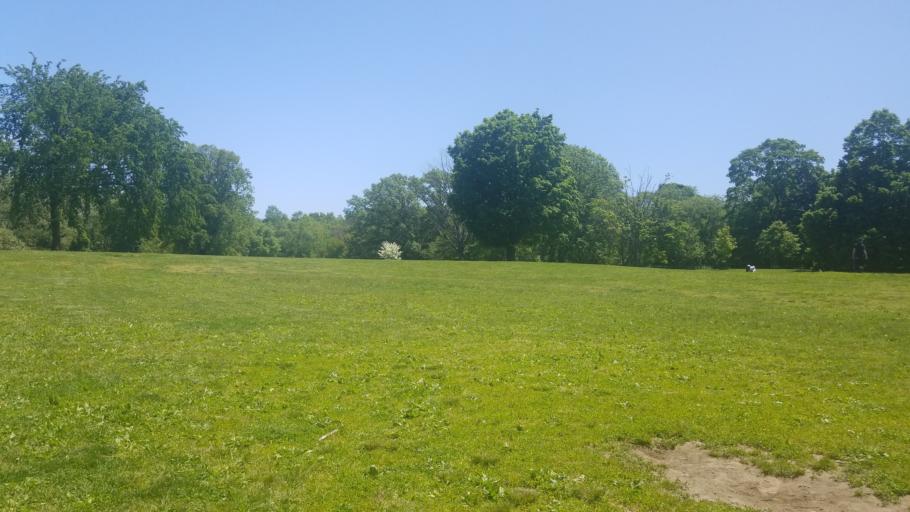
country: US
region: New York
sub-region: Kings County
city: Brooklyn
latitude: 40.6599
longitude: -73.9700
